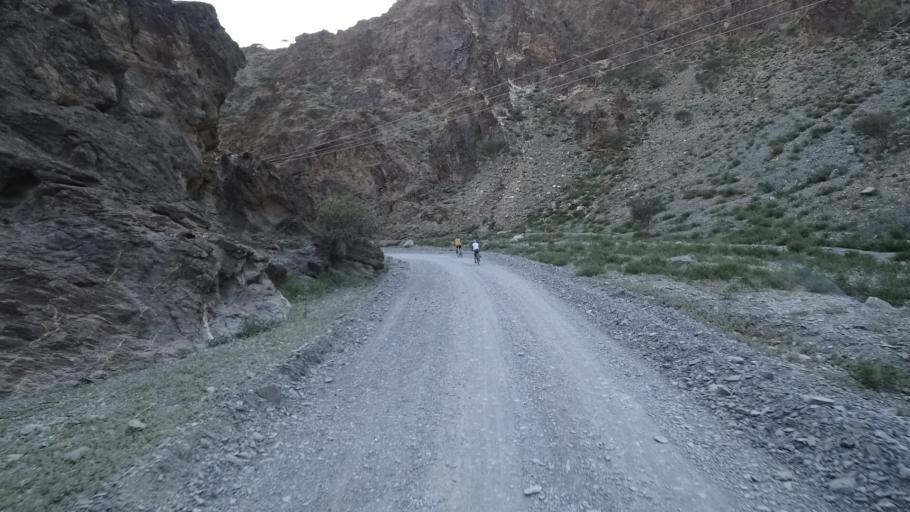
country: OM
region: Al Batinah
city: Rustaq
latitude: 23.2596
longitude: 57.3949
